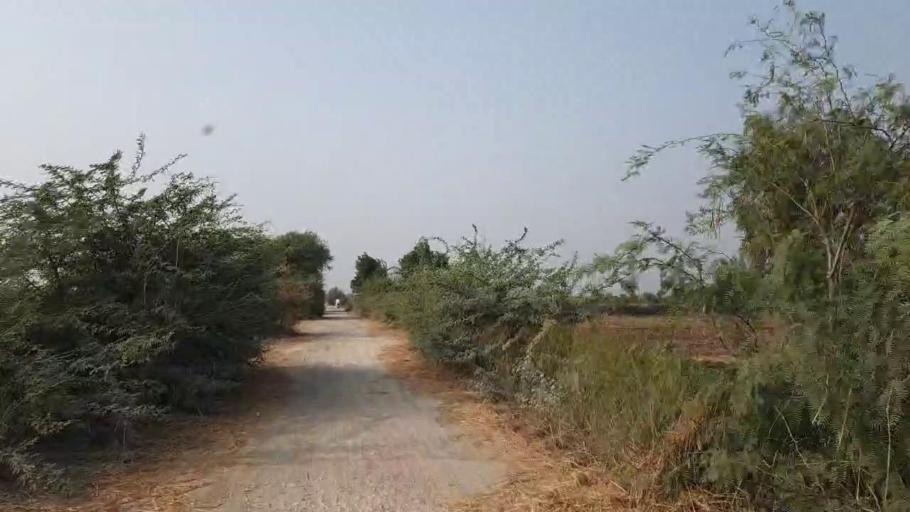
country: PK
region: Sindh
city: Tando Muhammad Khan
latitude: 25.0816
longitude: 68.5875
